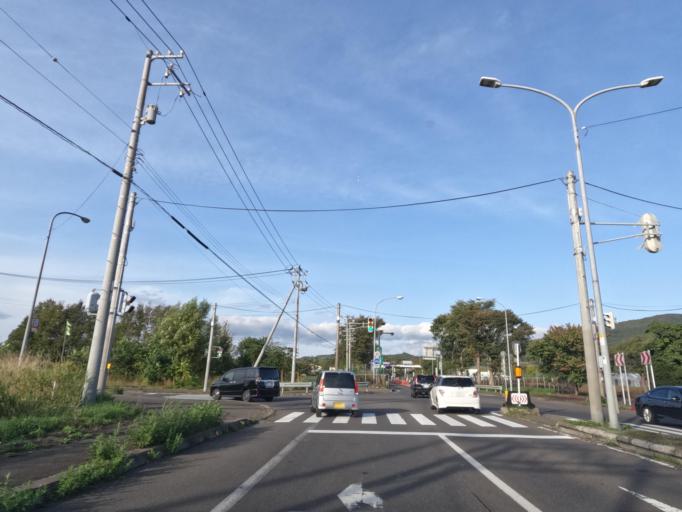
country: JP
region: Hokkaido
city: Date
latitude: 42.4793
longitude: 140.8875
